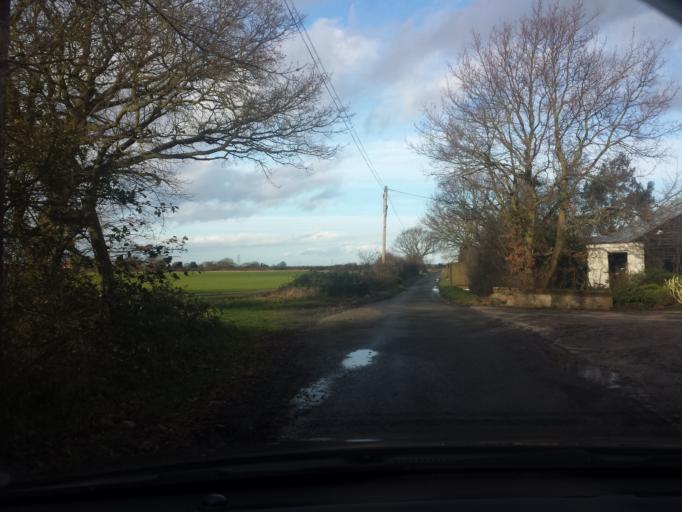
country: GB
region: England
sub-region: Essex
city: Great Bentley
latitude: 51.8972
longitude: 1.0557
